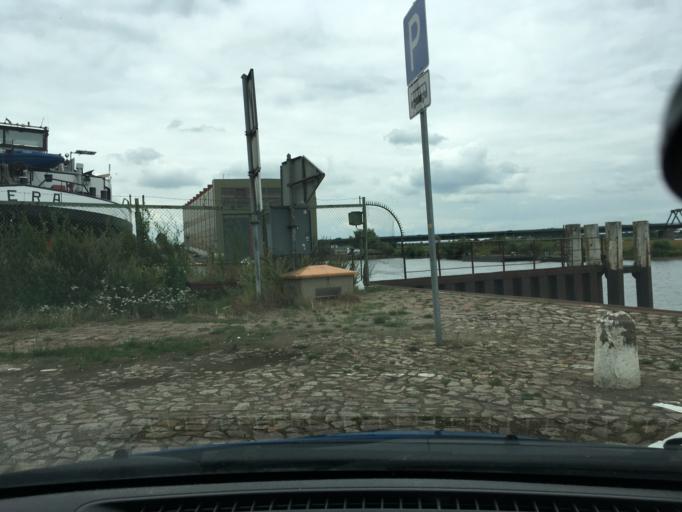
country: DE
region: Schleswig-Holstein
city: Lauenburg
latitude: 53.3702
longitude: 10.5600
